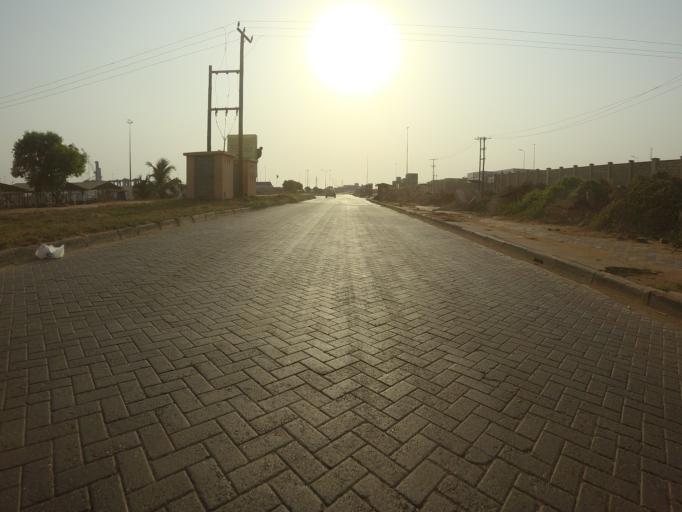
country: GH
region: Greater Accra
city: Tema
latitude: 5.6197
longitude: -0.0157
